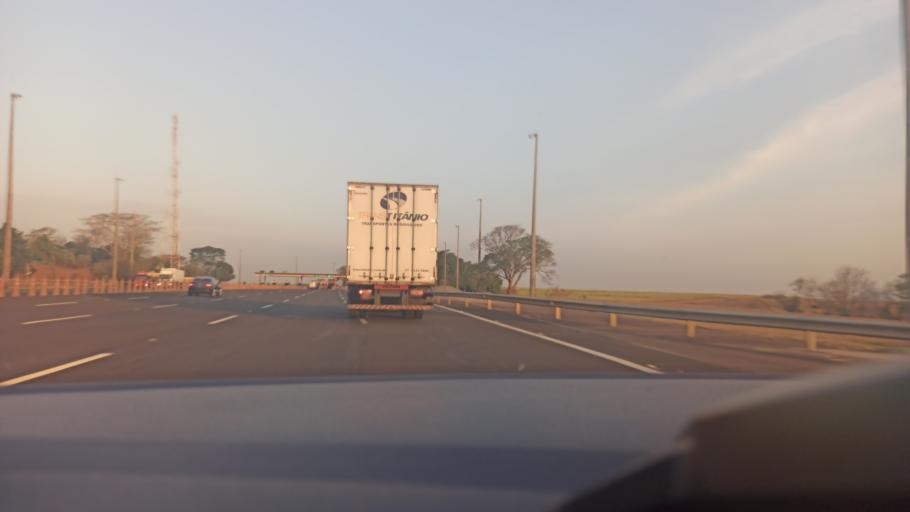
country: BR
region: Sao Paulo
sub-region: Santa Adelia
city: Santa Adelia
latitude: -21.3817
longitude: -48.7341
